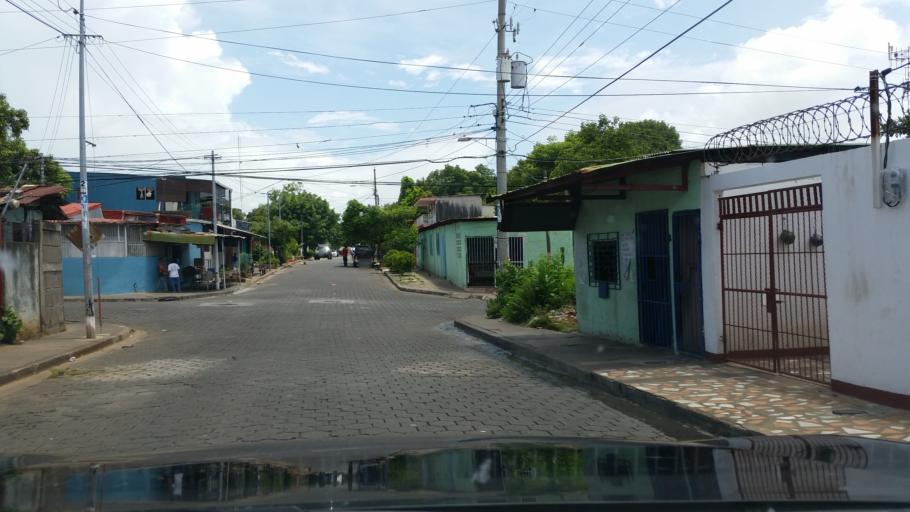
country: NI
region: Managua
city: Managua
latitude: 12.1299
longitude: -86.2575
